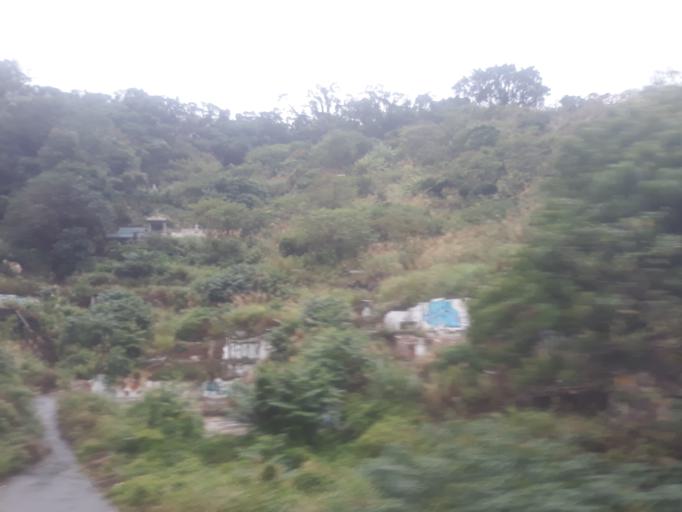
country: TW
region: Taipei
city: Taipei
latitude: 25.0153
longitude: 121.5603
